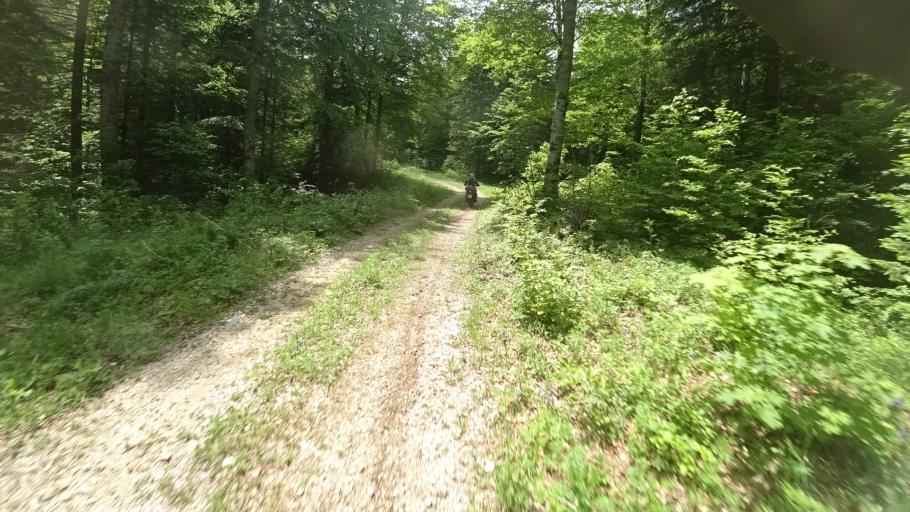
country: HR
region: Zadarska
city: Gracac
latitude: 44.4751
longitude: 15.8941
